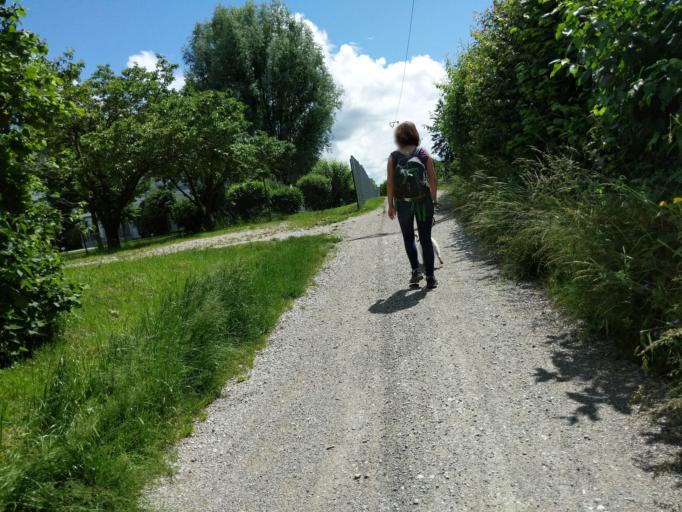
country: DE
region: Bavaria
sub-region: Upper Bavaria
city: Herrsching am Ammersee
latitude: 48.0042
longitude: 11.1720
